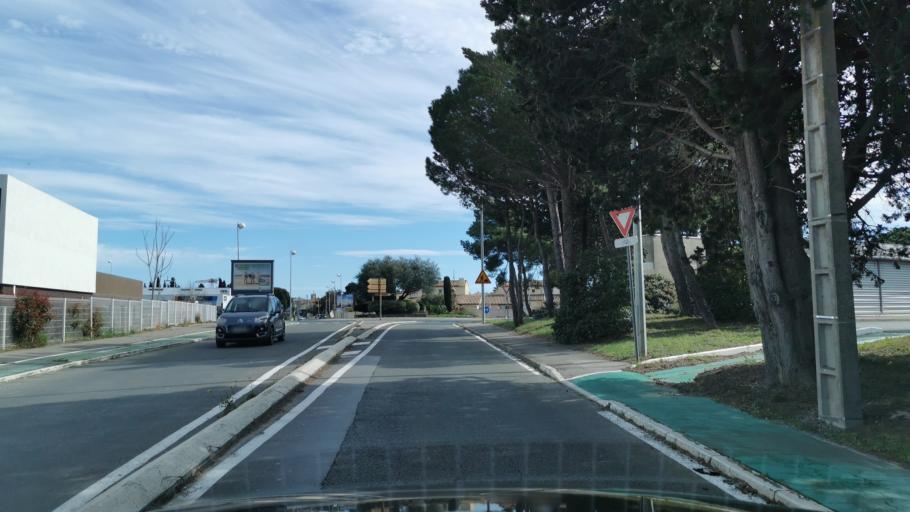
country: FR
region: Languedoc-Roussillon
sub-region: Departement de l'Aude
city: Narbonne
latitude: 43.1902
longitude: 2.9843
